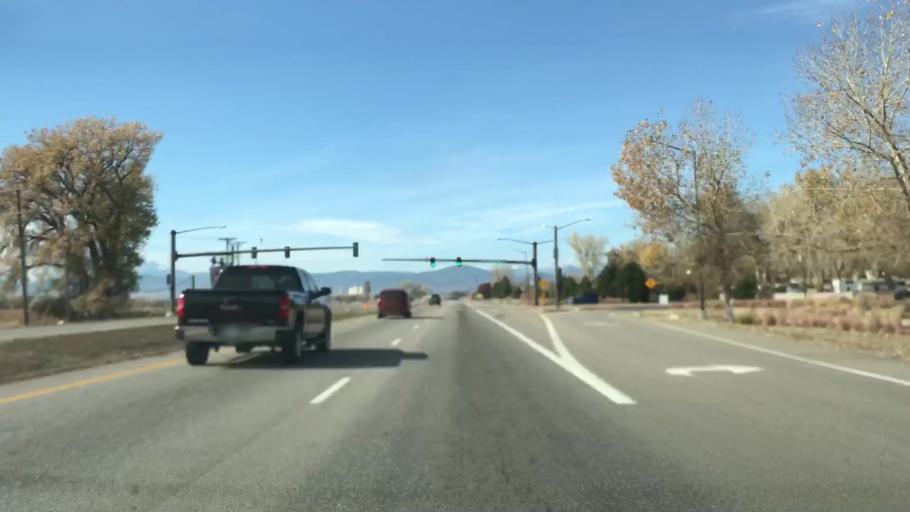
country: US
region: Colorado
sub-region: Larimer County
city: Loveland
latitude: 40.4073
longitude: -105.0103
